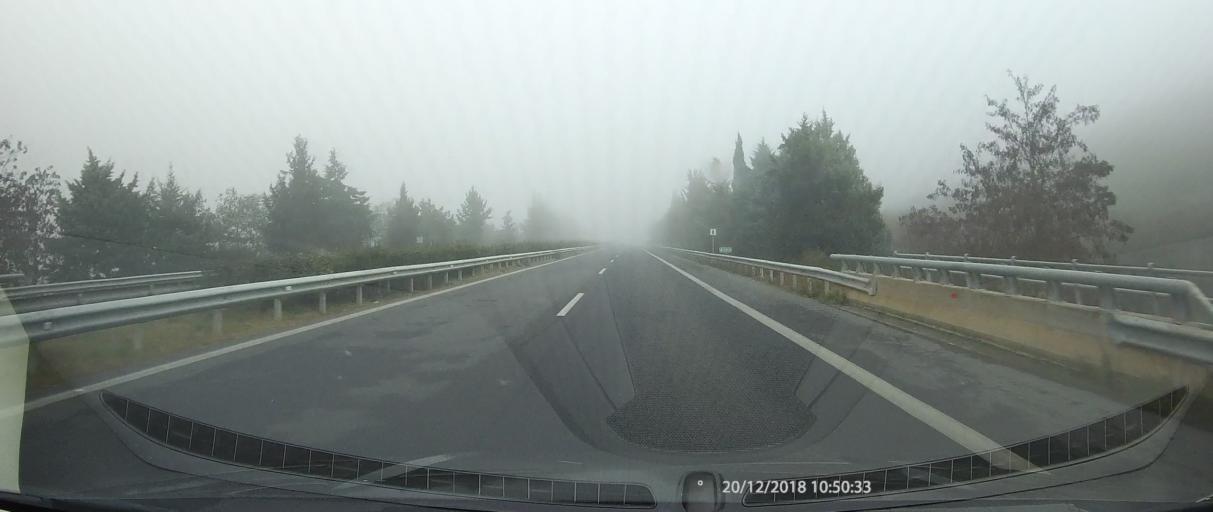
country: GR
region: Peloponnese
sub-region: Nomos Arkadias
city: Tripoli
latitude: 37.5656
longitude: 22.4257
